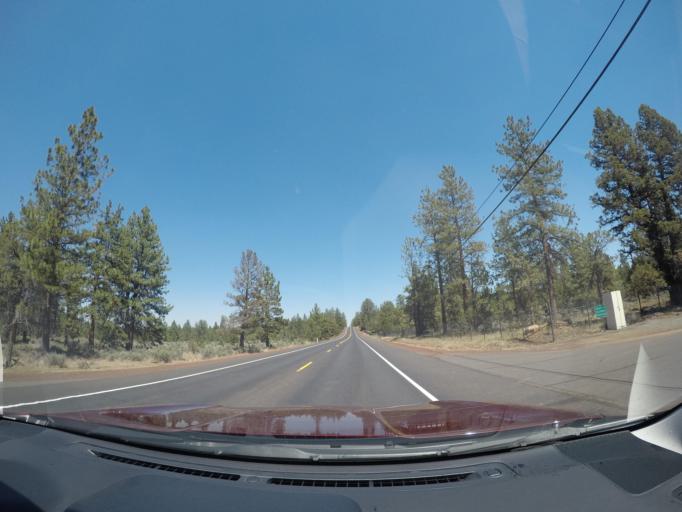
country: US
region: Oregon
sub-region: Deschutes County
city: Sisters
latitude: 44.2872
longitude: -121.5104
